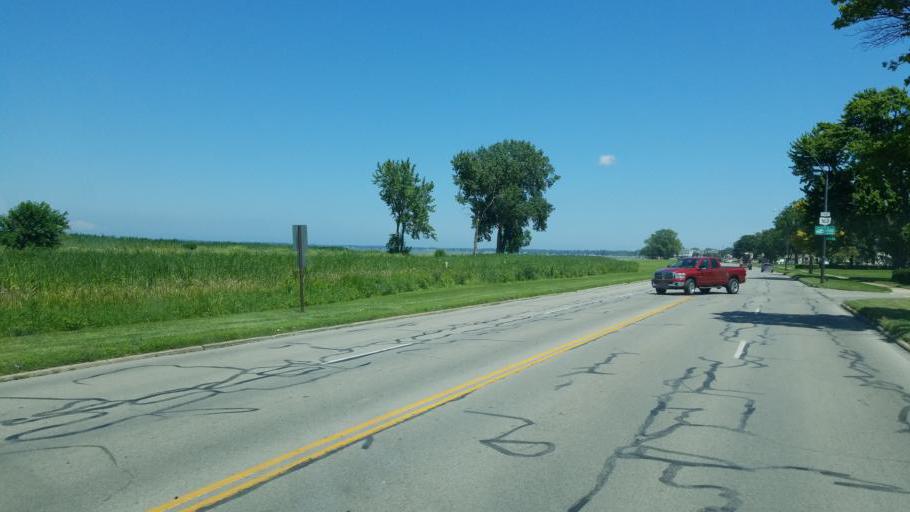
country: US
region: Ohio
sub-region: Ottawa County
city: Port Clinton
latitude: 41.5136
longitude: -82.9309
